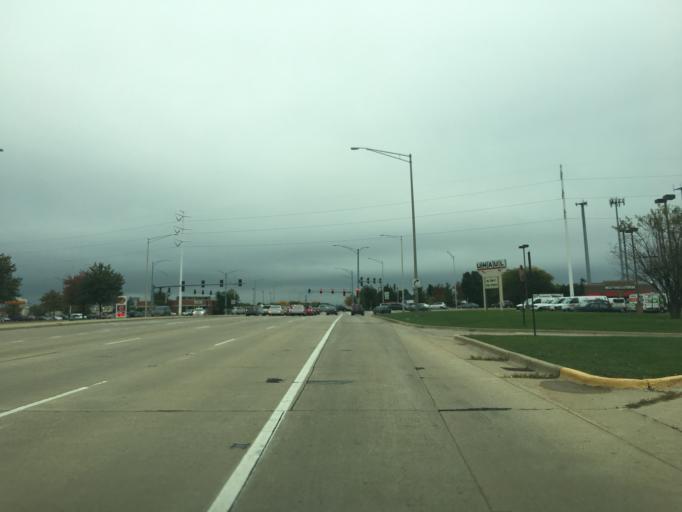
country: US
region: Illinois
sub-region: DuPage County
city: Naperville
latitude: 41.7526
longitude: -88.2074
